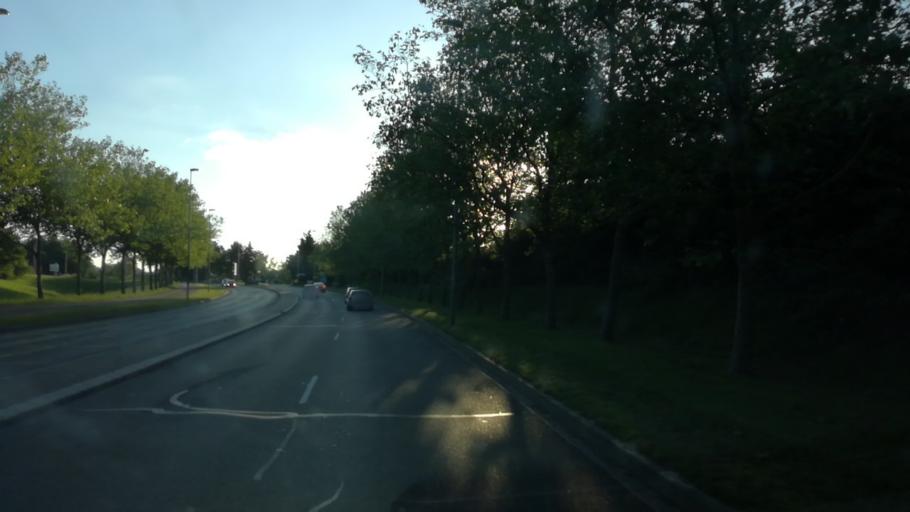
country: FR
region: Ile-de-France
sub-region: Departement des Yvelines
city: Elancourt
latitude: 48.7780
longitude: 1.9626
